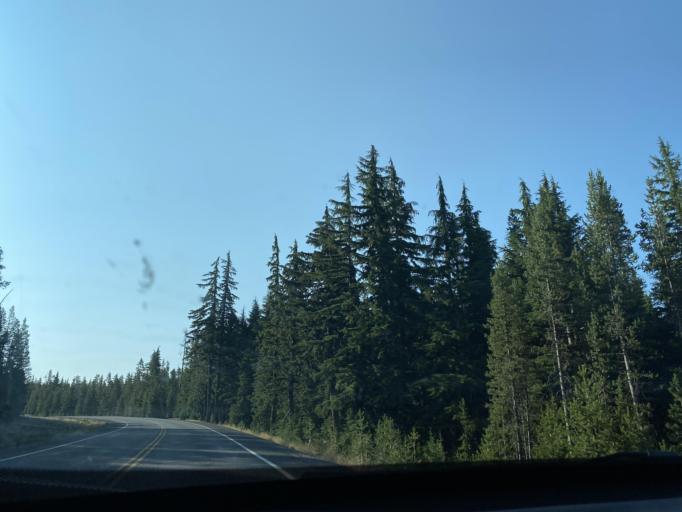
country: US
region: Oregon
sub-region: Deschutes County
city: Three Rivers
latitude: 43.7061
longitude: -121.2657
